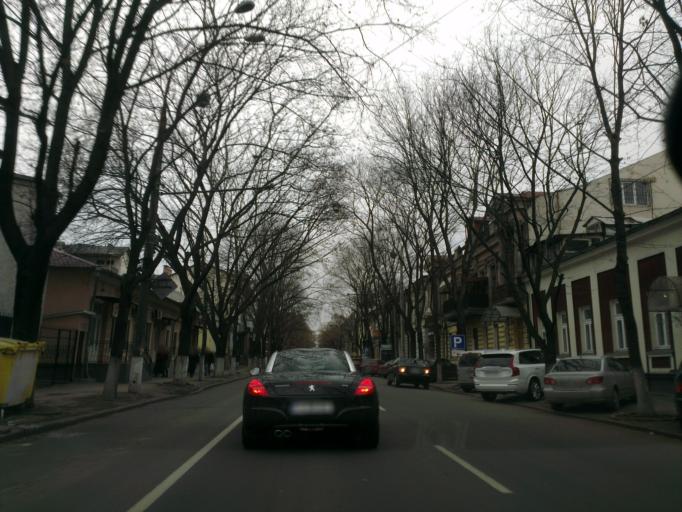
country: MD
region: Chisinau
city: Chisinau
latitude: 47.0189
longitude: 28.8322
